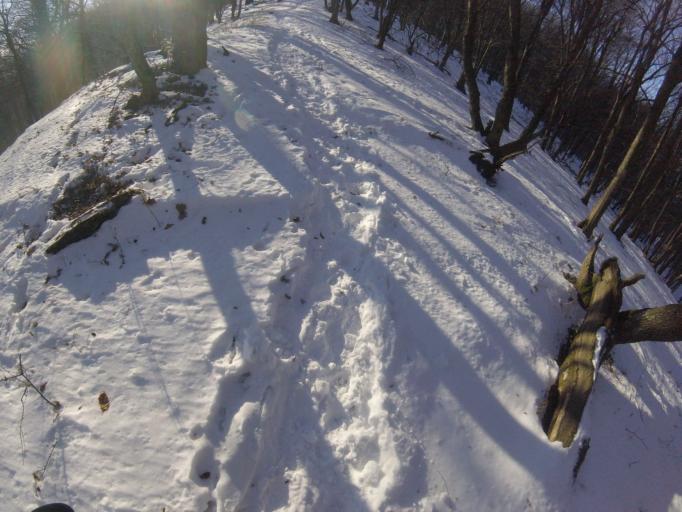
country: SK
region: Nitriansky
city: Sahy
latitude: 47.9778
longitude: 18.8867
